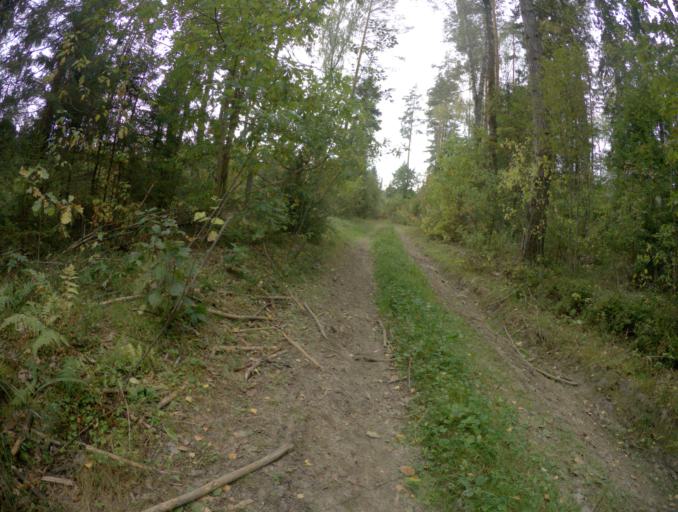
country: RU
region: Vladimir
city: Golovino
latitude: 55.9913
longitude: 40.4683
